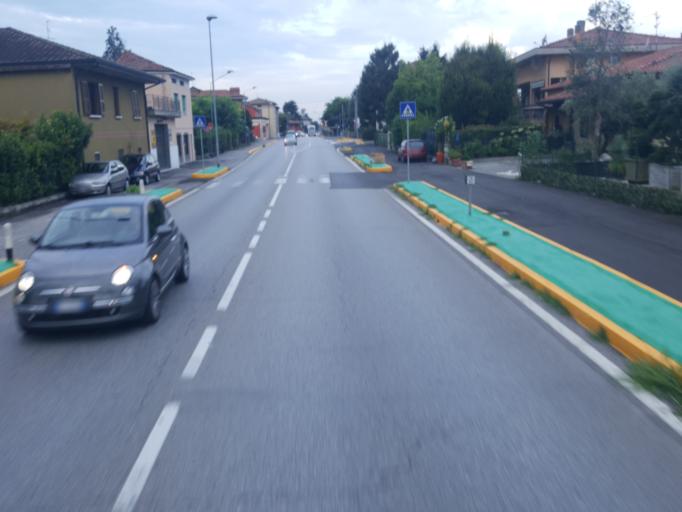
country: IT
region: Lombardy
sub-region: Provincia di Brescia
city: Roncadelle
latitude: 45.5248
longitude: 10.1557
